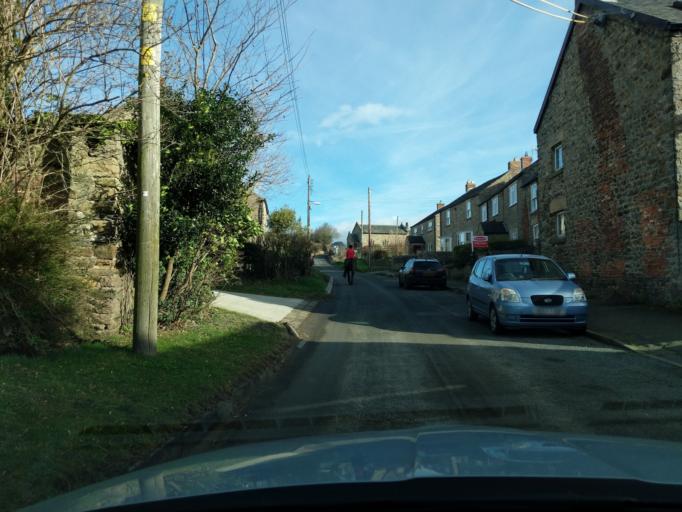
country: GB
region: England
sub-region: North Yorkshire
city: Catterick Garrison
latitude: 54.3291
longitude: -1.7082
